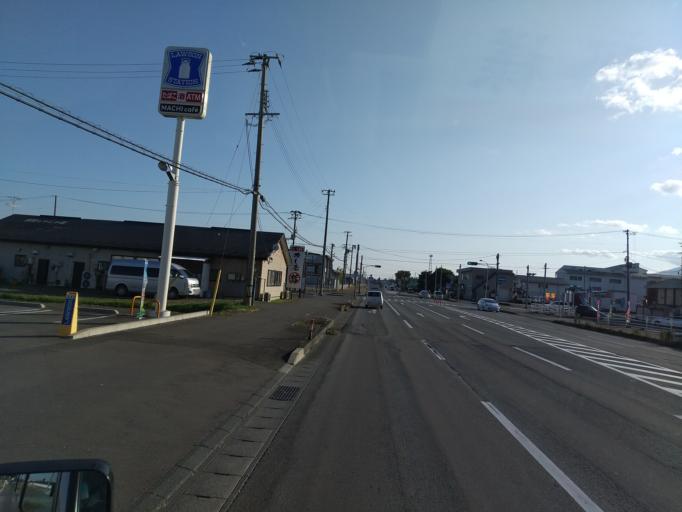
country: JP
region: Iwate
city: Morioka-shi
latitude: 39.6568
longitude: 141.1138
